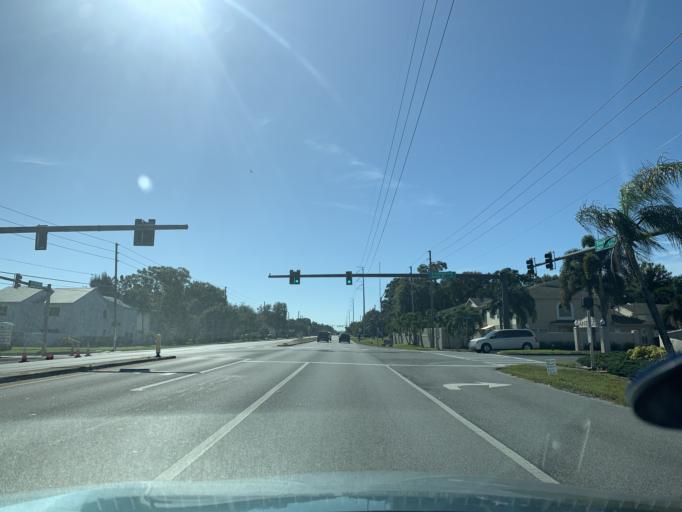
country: US
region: Florida
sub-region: Pinellas County
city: Seminole
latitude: 27.8607
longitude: -82.7624
